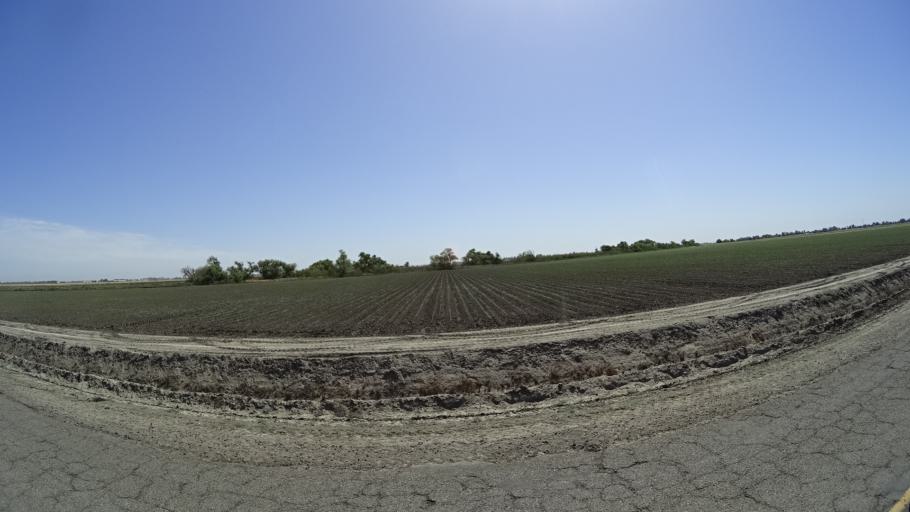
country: US
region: California
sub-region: Kings County
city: Stratford
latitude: 36.2083
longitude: -119.8342
